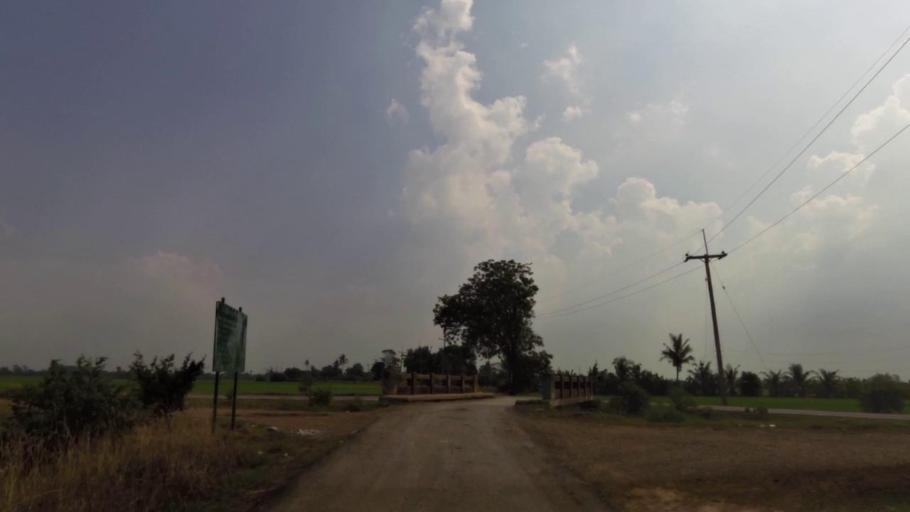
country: TH
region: Ang Thong
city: Pho Thong
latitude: 14.6194
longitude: 100.4020
